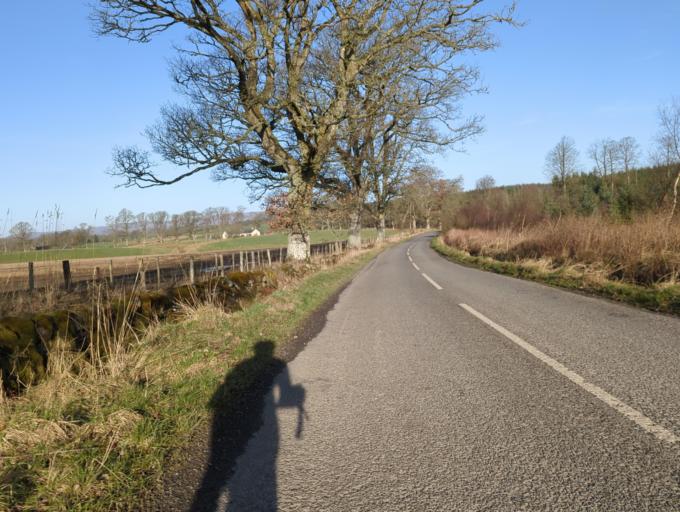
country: GB
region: Scotland
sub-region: Perth and Kinross
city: Methven
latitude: 56.4563
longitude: -3.5843
